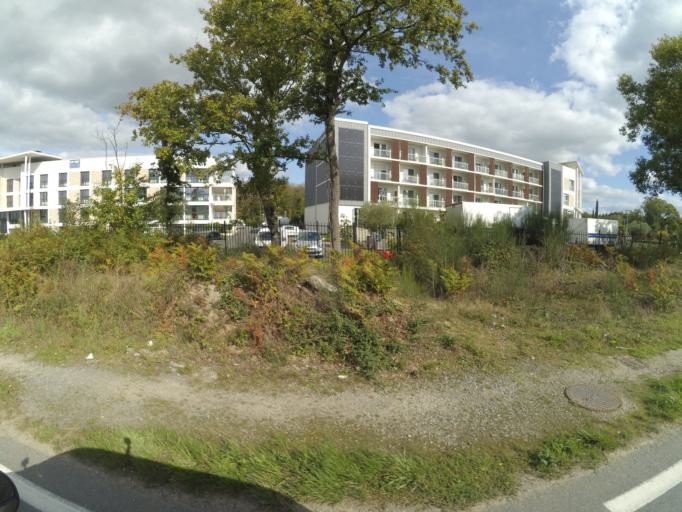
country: FR
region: Pays de la Loire
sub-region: Departement de la Loire-Atlantique
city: Carquefou
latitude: 47.2934
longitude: -1.4719
